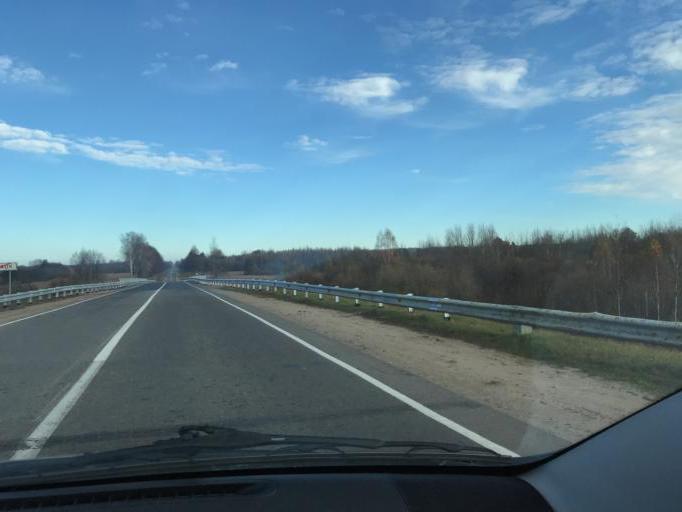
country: BY
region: Vitebsk
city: Haradok
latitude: 55.5017
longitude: 29.9680
